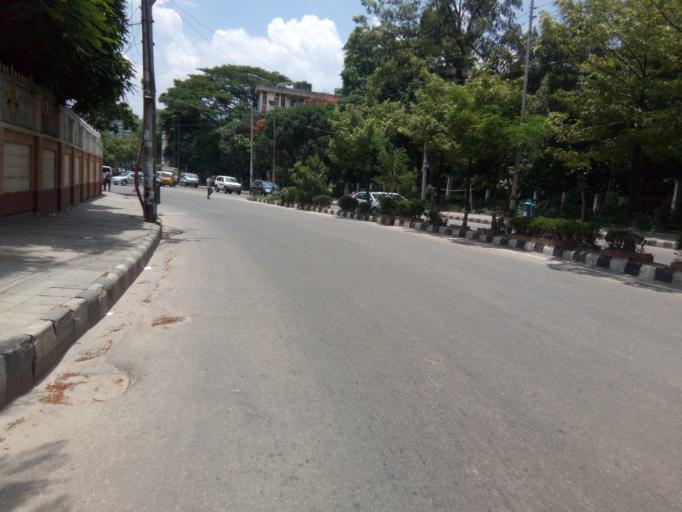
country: BD
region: Dhaka
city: Paltan
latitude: 23.7438
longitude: 90.4054
